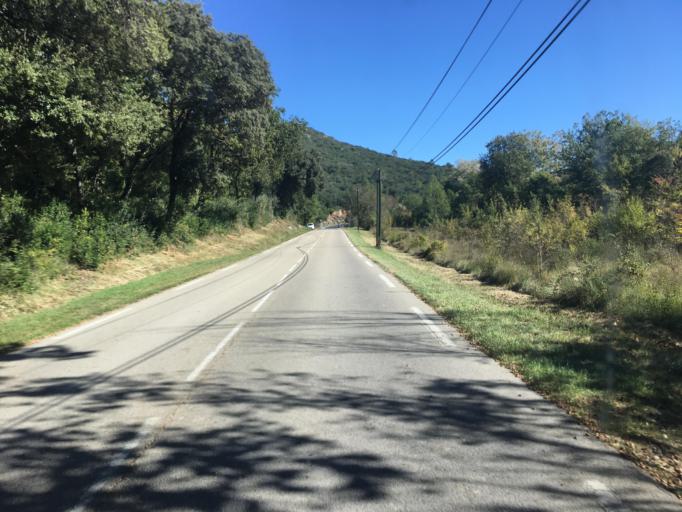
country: FR
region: Languedoc-Roussillon
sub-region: Departement du Gard
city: Quissac
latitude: 43.9203
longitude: 4.0248
